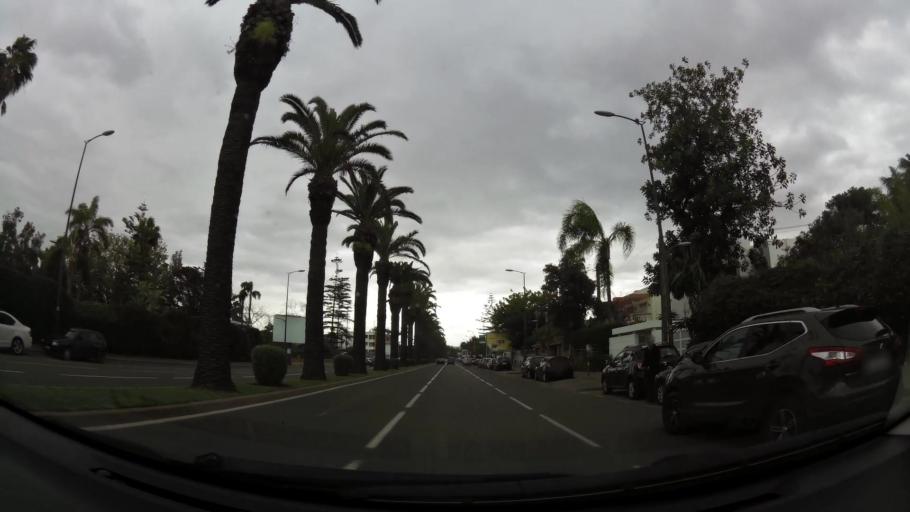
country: MA
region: Grand Casablanca
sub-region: Casablanca
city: Casablanca
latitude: 33.5818
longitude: -7.6603
